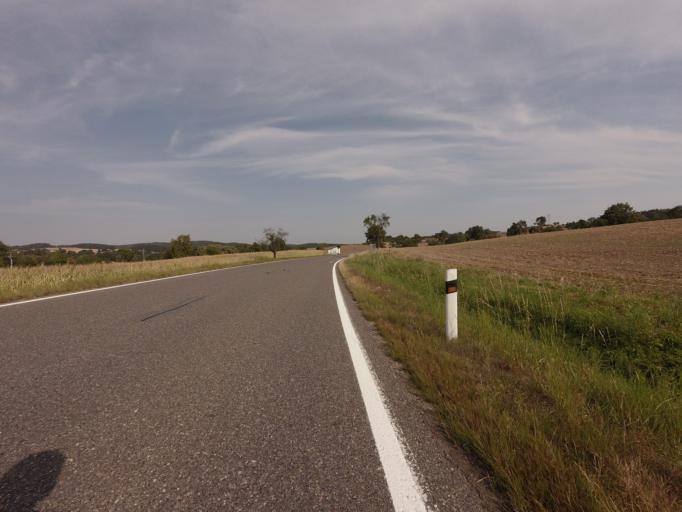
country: CZ
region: Central Bohemia
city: Petrovice
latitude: 49.5123
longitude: 14.3596
